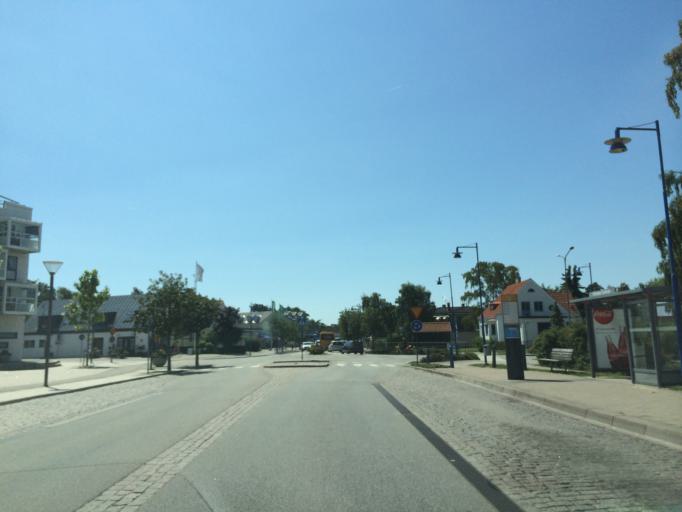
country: SE
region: Skane
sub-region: Vellinge Kommun
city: Hollviken
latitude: 55.4187
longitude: 12.9530
